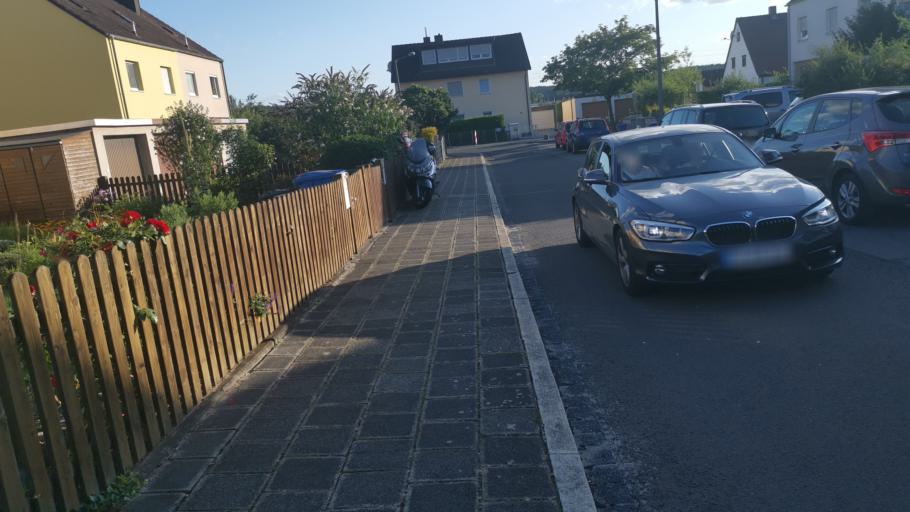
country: DE
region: Bavaria
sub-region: Regierungsbezirk Mittelfranken
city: Furth
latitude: 49.4763
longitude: 10.9552
